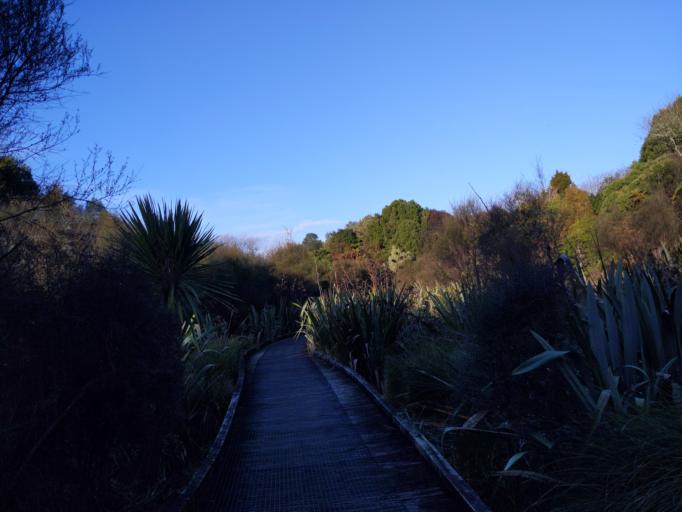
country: NZ
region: Waikato
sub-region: Hamilton City
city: Hamilton
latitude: -37.7383
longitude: 175.2780
